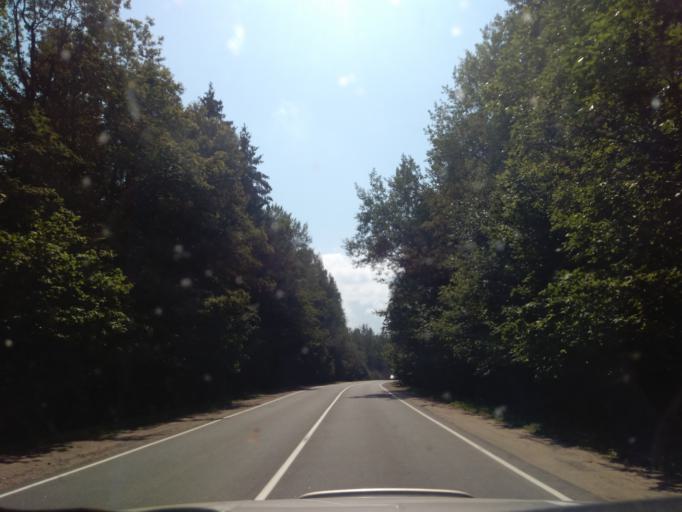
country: BY
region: Minsk
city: Khatsyezhyna
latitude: 53.9057
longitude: 27.2603
